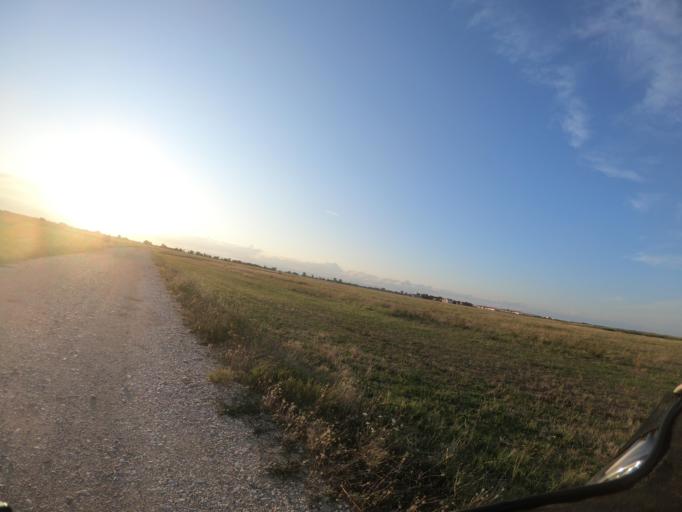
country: HU
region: Jasz-Nagykun-Szolnok
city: Tiszafured
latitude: 47.7311
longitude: 20.7945
